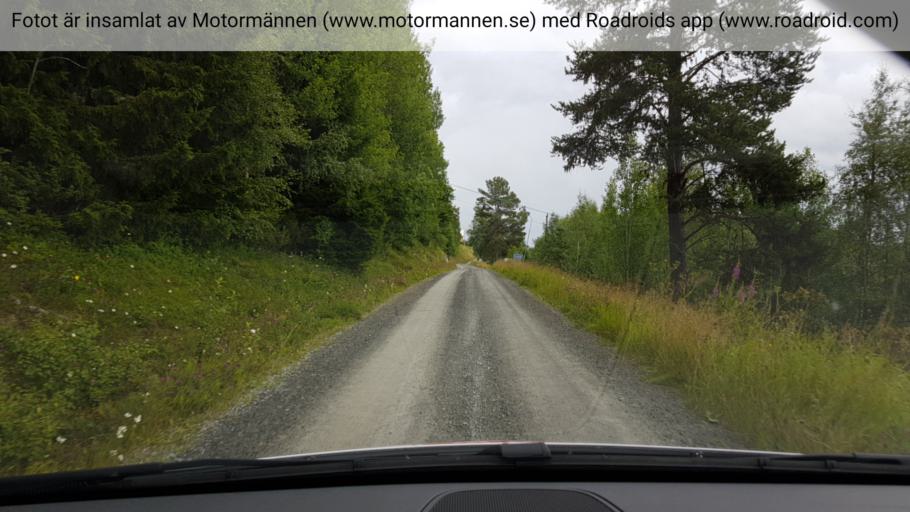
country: SE
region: Jaemtland
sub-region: Krokoms Kommun
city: Valla
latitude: 63.5828
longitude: 13.9815
